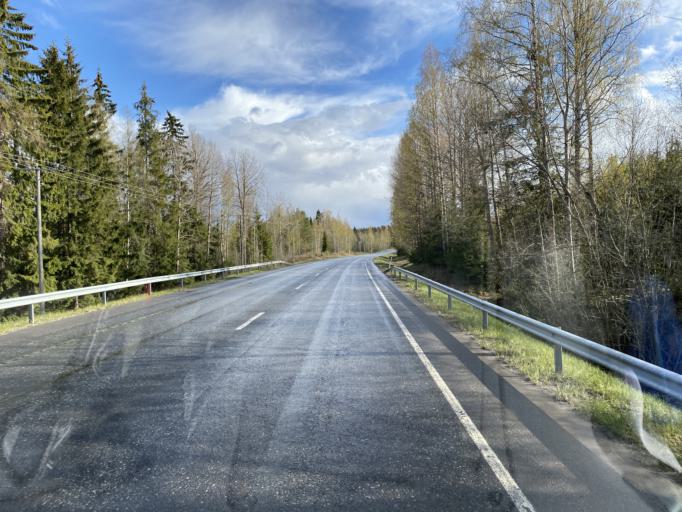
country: FI
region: Pirkanmaa
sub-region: Etelae-Pirkanmaa
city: Viiala
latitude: 61.2335
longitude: 23.7417
